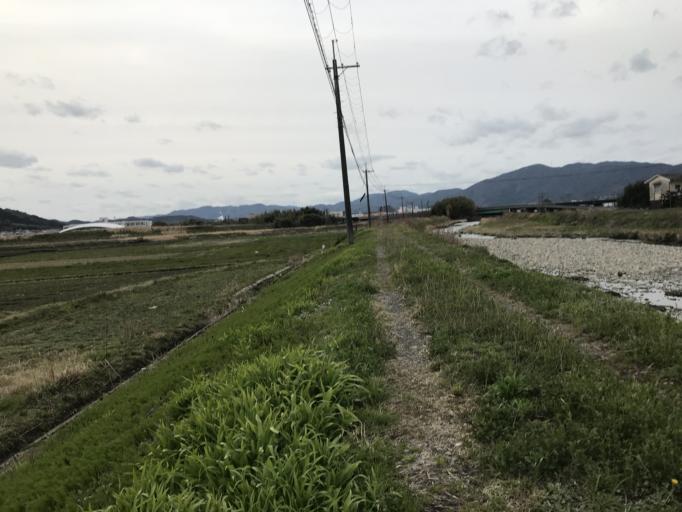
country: JP
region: Kyoto
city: Kameoka
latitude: 35.0183
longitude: 135.5488
